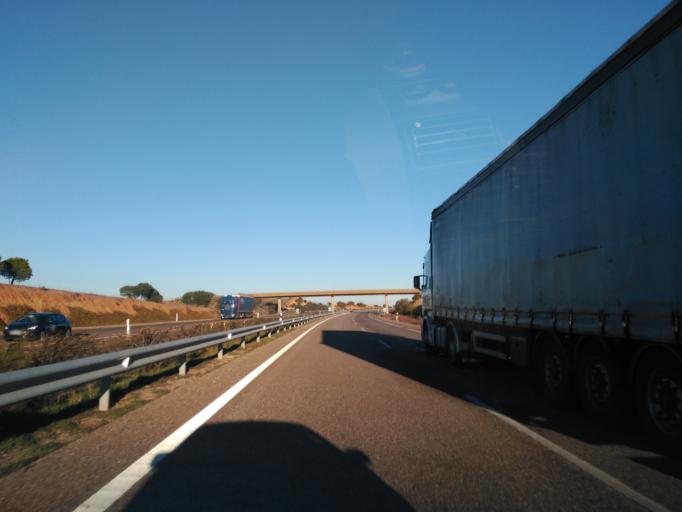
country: ES
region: Castille and Leon
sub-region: Provincia de Salamanca
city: Parada de Rubiales
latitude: 41.1618
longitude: -5.4405
